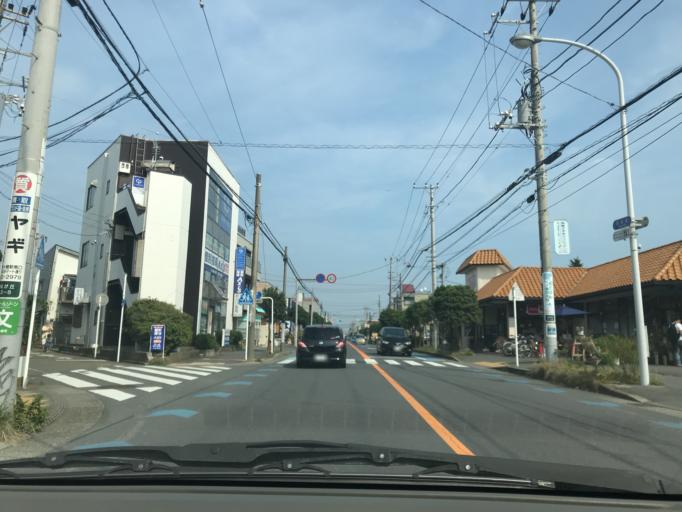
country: JP
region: Kanagawa
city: Chigasaki
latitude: 35.3253
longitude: 139.4233
